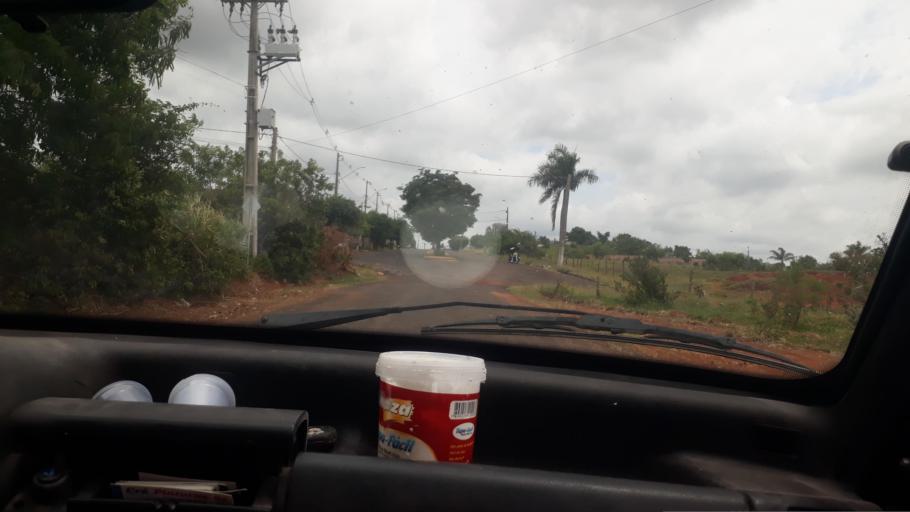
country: BR
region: Sao Paulo
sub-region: Regente Feijo
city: Regente Feijo
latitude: -22.2331
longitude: -51.3004
